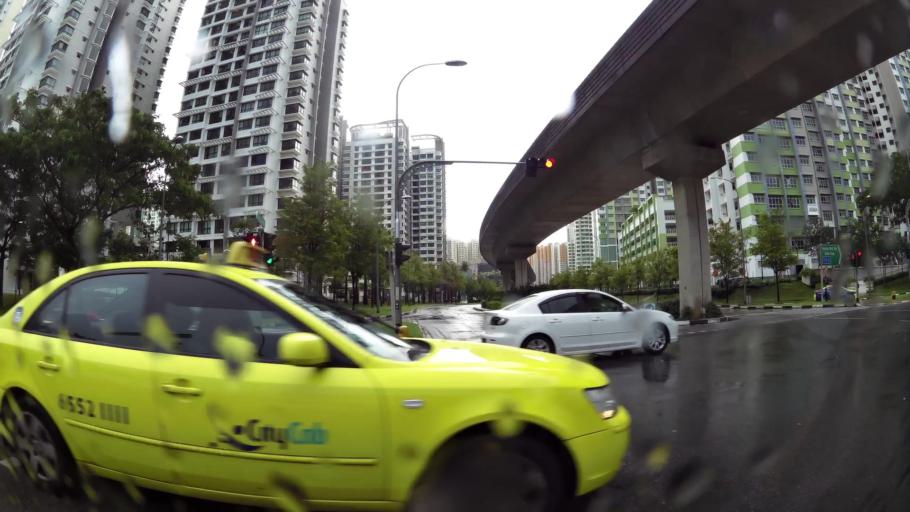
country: MY
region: Johor
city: Kampung Pasir Gudang Baru
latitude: 1.3950
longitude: 103.8759
